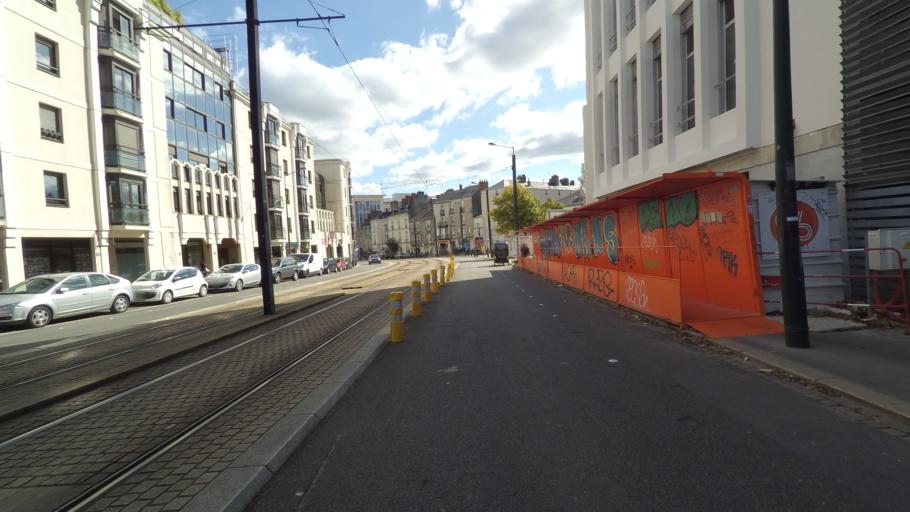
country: FR
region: Pays de la Loire
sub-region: Departement de la Loire-Atlantique
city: Nantes
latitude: 47.2199
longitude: -1.5618
